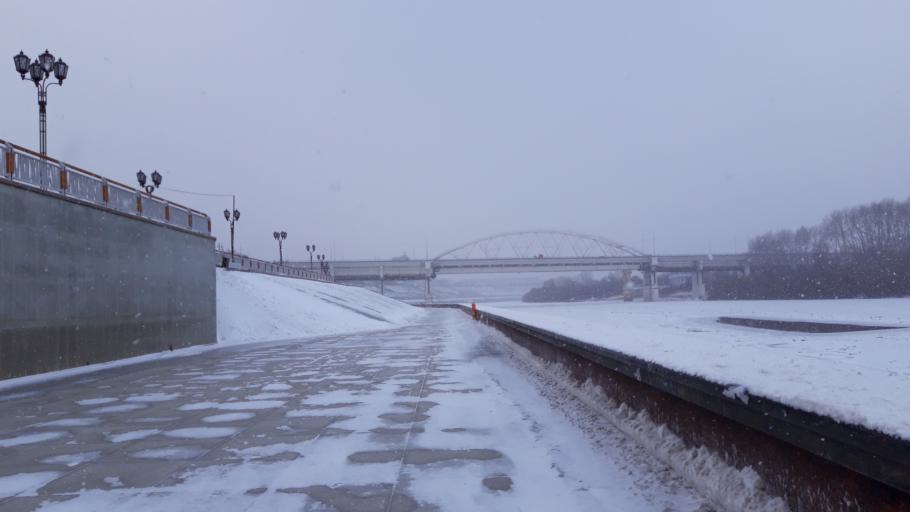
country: RU
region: Tjumen
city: Tyumen
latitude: 57.1621
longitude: 65.5469
